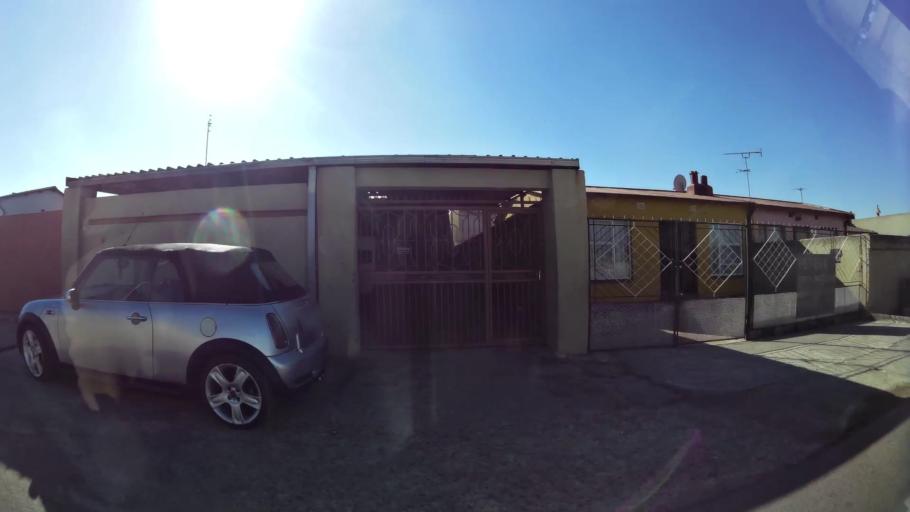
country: ZA
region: Gauteng
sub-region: City of Johannesburg Metropolitan Municipality
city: Roodepoort
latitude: -26.2215
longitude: 27.9151
